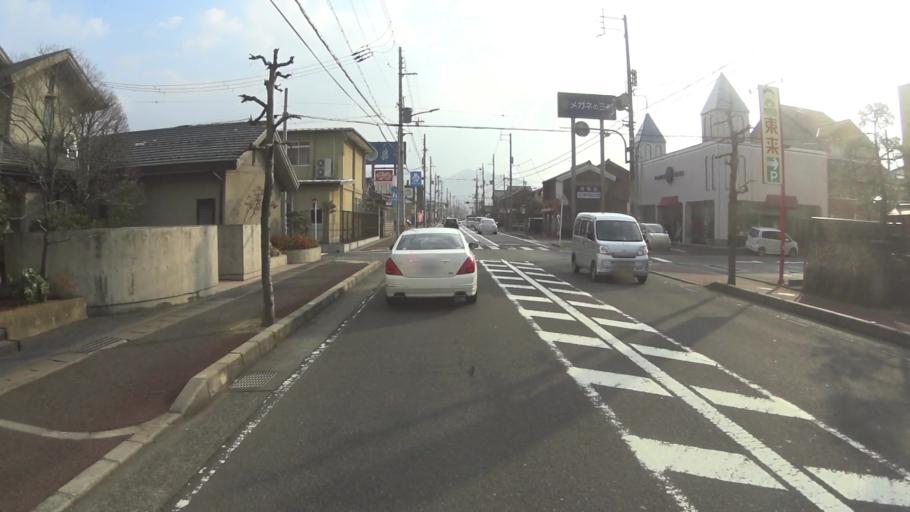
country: JP
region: Kyoto
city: Maizuru
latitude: 35.4693
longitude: 135.3973
